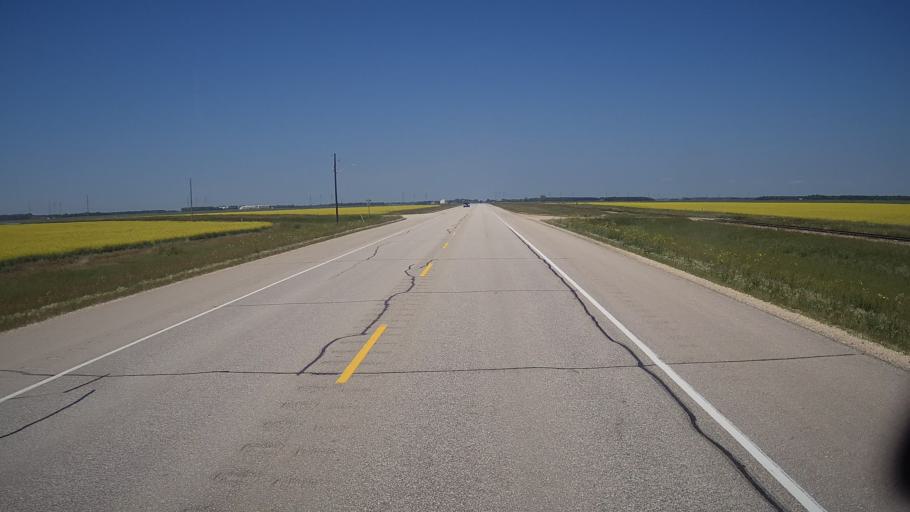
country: CA
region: Manitoba
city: Stonewall
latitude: 50.0337
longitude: -97.3957
